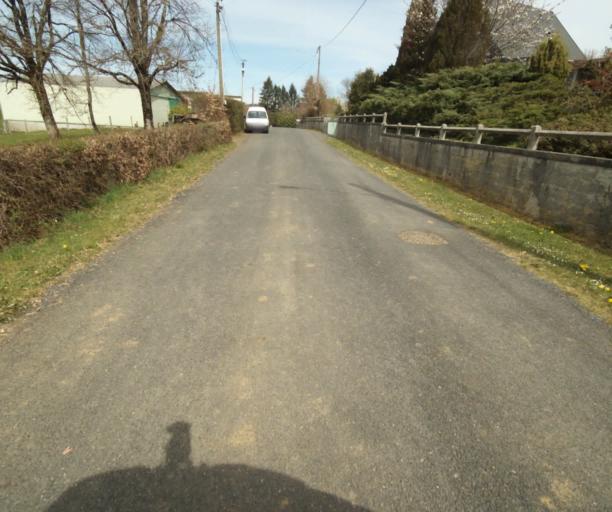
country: FR
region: Limousin
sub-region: Departement de la Correze
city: Naves
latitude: 45.3077
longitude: 1.7748
